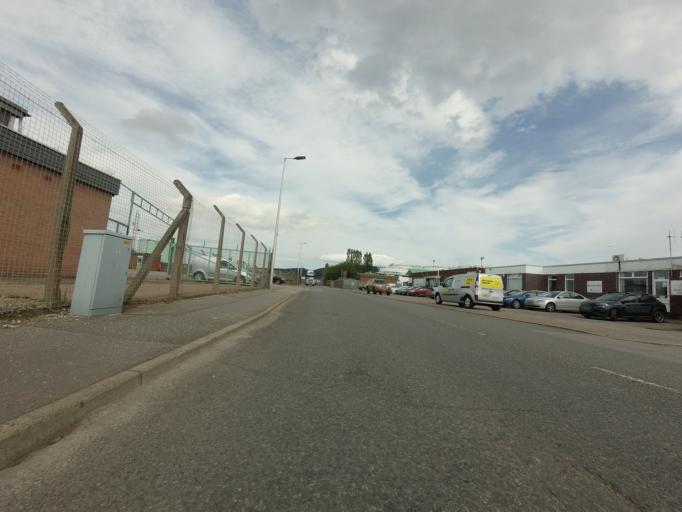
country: GB
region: Scotland
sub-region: Highland
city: Inverness
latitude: 57.4867
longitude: -4.2286
